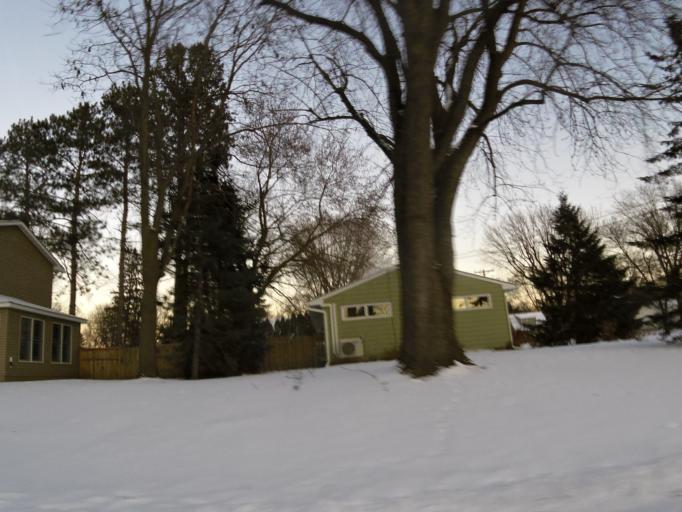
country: US
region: Minnesota
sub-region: Washington County
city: Stillwater
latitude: 45.0512
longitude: -92.8216
